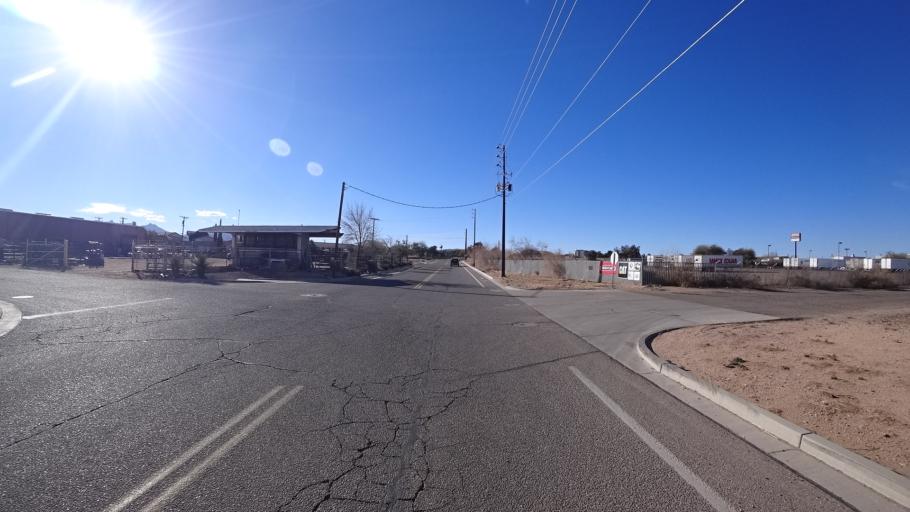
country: US
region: Arizona
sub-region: Mohave County
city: New Kingman-Butler
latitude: 35.2209
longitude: -114.0115
